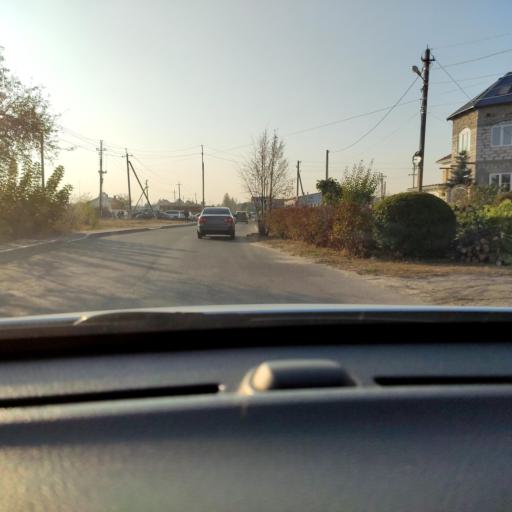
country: RU
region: Voronezj
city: Somovo
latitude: 51.6852
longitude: 39.3209
